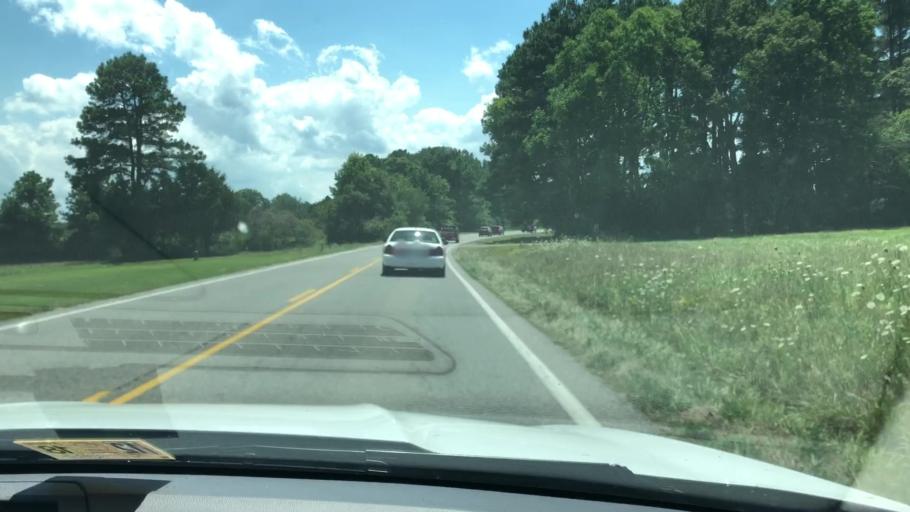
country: US
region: Virginia
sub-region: Middlesex County
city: Deltaville
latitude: 37.6006
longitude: -76.4425
